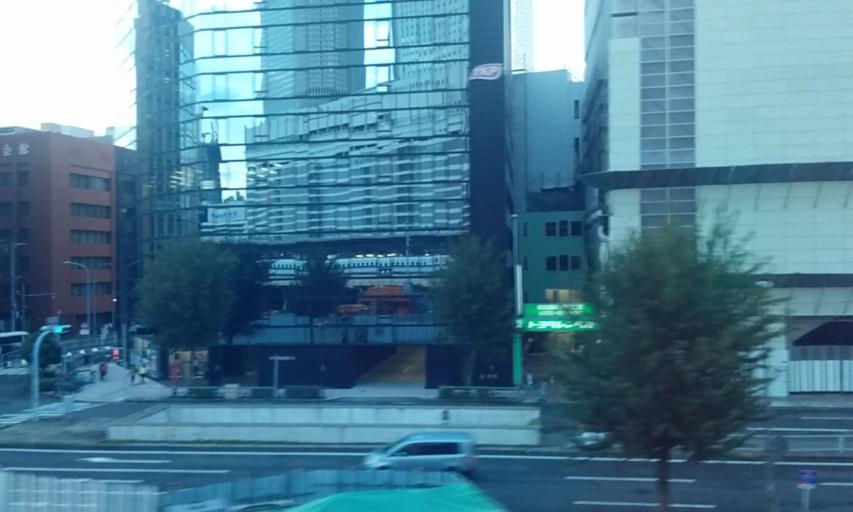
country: JP
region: Aichi
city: Nagoya-shi
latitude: 35.1720
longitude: 136.8800
